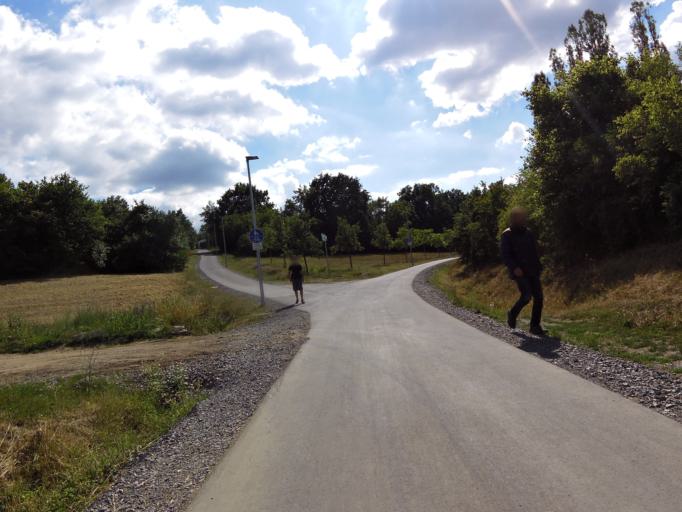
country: DE
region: Bavaria
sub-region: Regierungsbezirk Unterfranken
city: Gerbrunn
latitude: 49.7863
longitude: 9.9946
